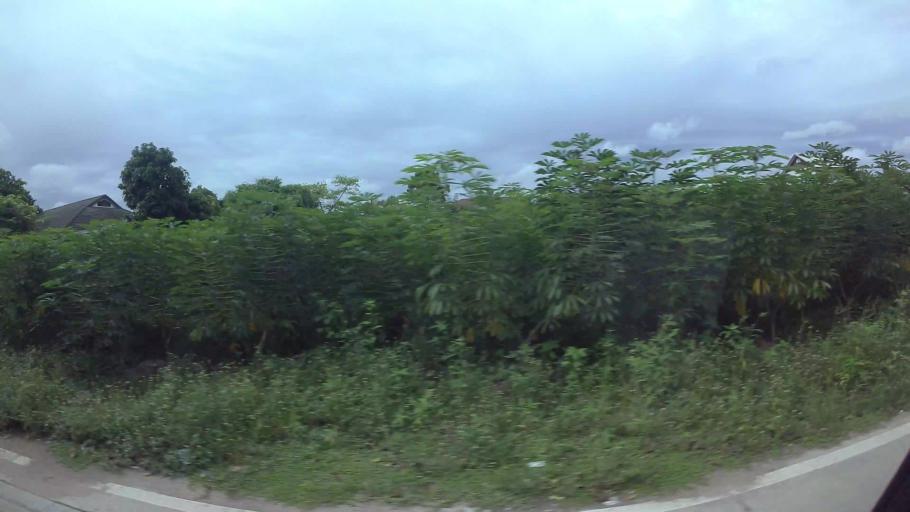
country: TH
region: Chon Buri
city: Si Racha
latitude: 13.1508
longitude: 100.9753
